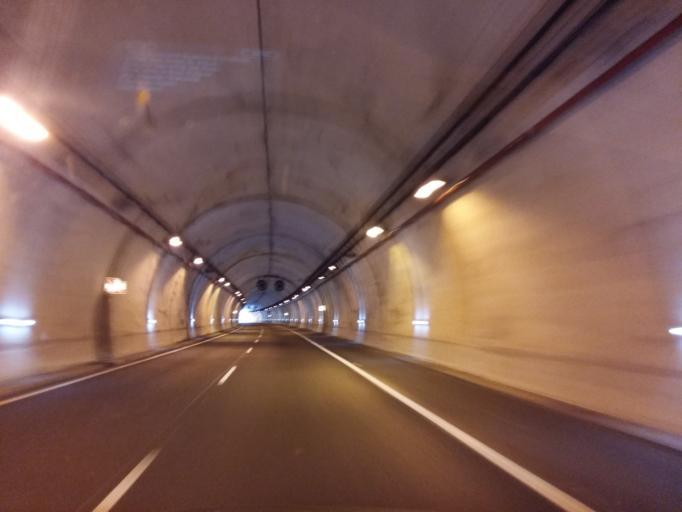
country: ES
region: Asturias
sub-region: Province of Asturias
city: Ribadesella
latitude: 43.4434
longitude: -5.0929
